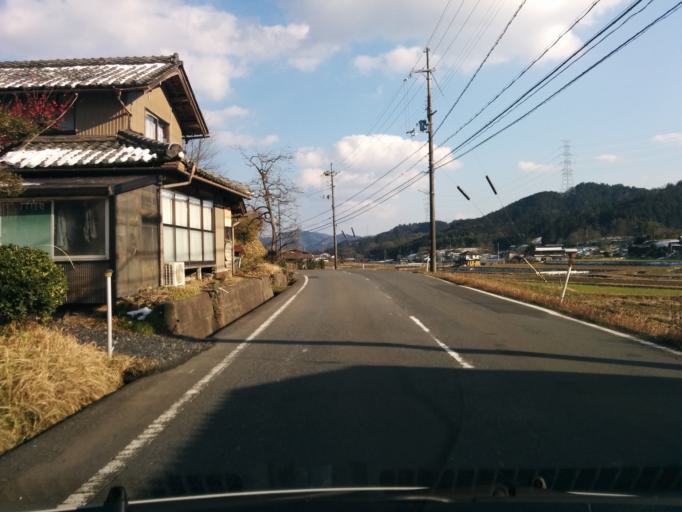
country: JP
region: Kyoto
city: Ayabe
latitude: 35.3672
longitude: 135.1970
